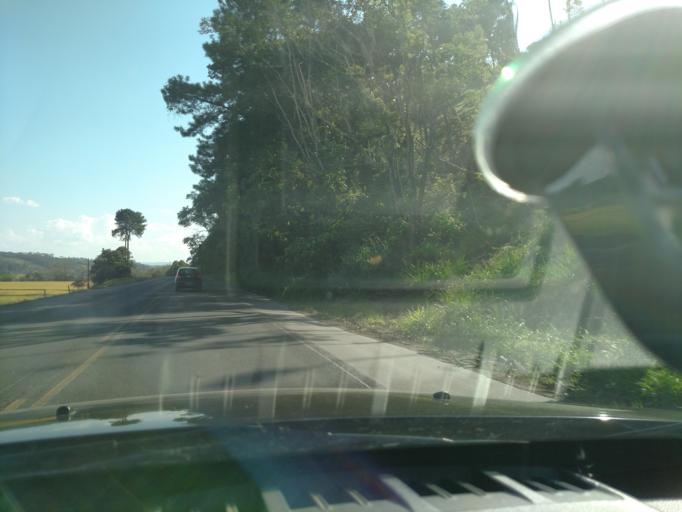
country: BR
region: Santa Catarina
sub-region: Rio Do Sul
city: Rio do Sul
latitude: -27.2690
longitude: -49.7304
